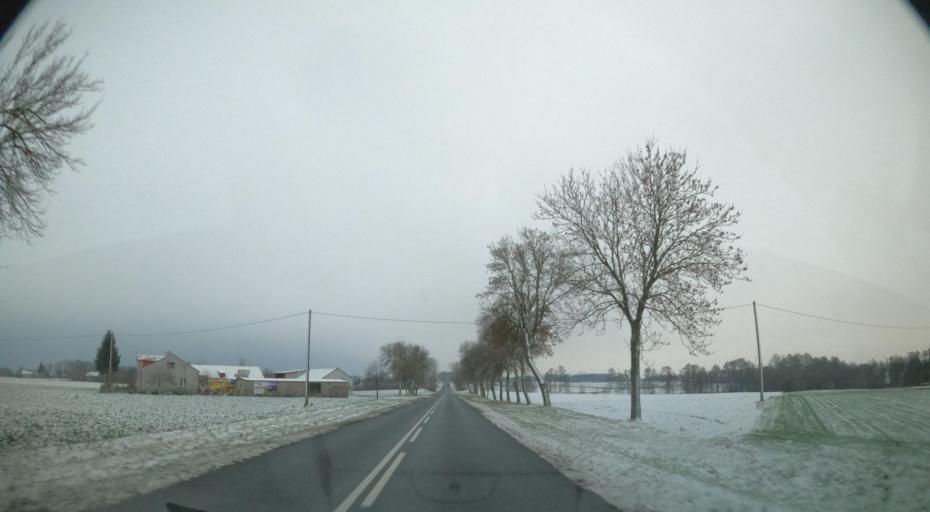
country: PL
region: Kujawsko-Pomorskie
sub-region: Powiat lipnowski
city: Dobrzyn nad Wisla
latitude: 52.6554
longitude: 19.3925
